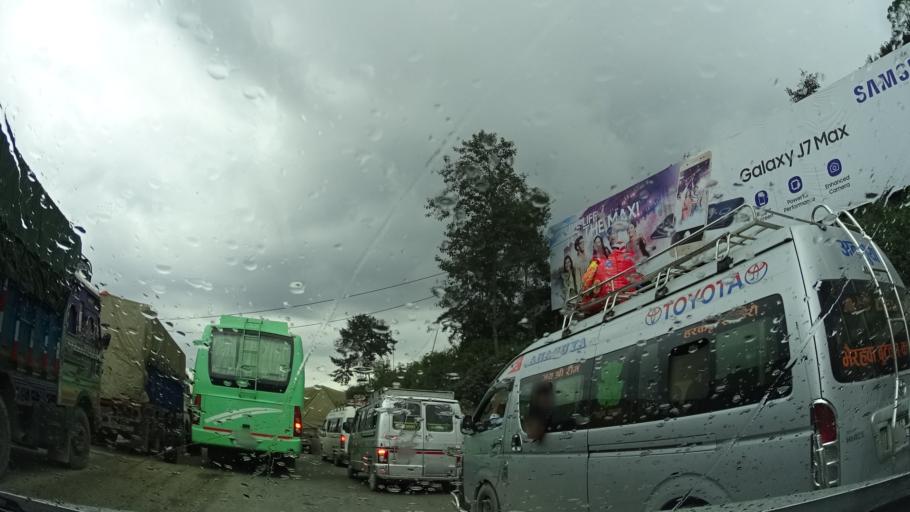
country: NP
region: Central Region
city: Kirtipur
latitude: 27.7057
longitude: 85.2061
